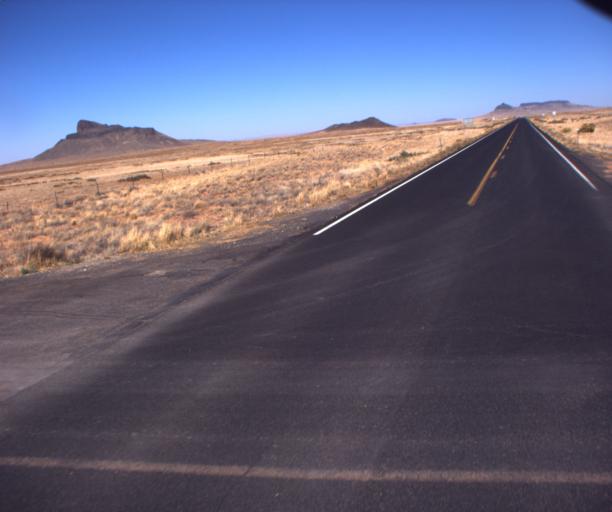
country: US
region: Arizona
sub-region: Navajo County
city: Dilkon
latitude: 35.4483
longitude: -110.4237
